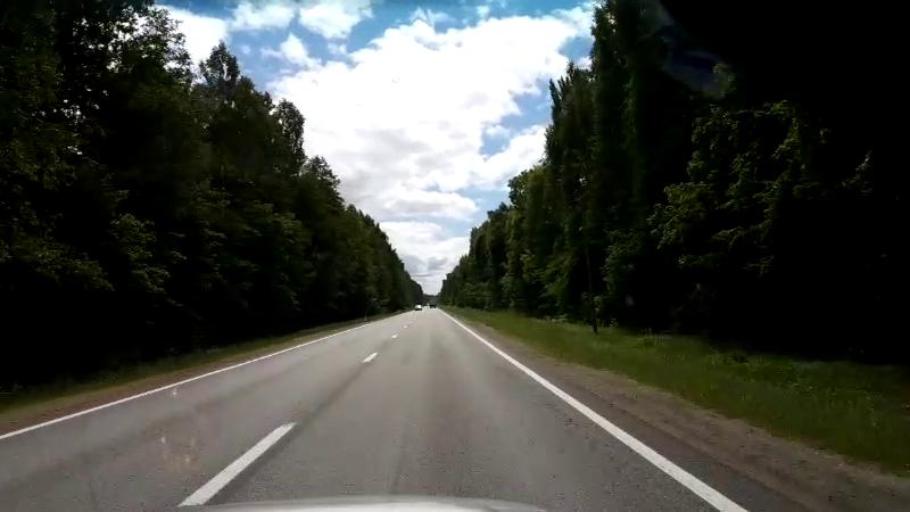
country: LV
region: Salacgrivas
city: Salacgriva
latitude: 57.5883
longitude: 24.4215
